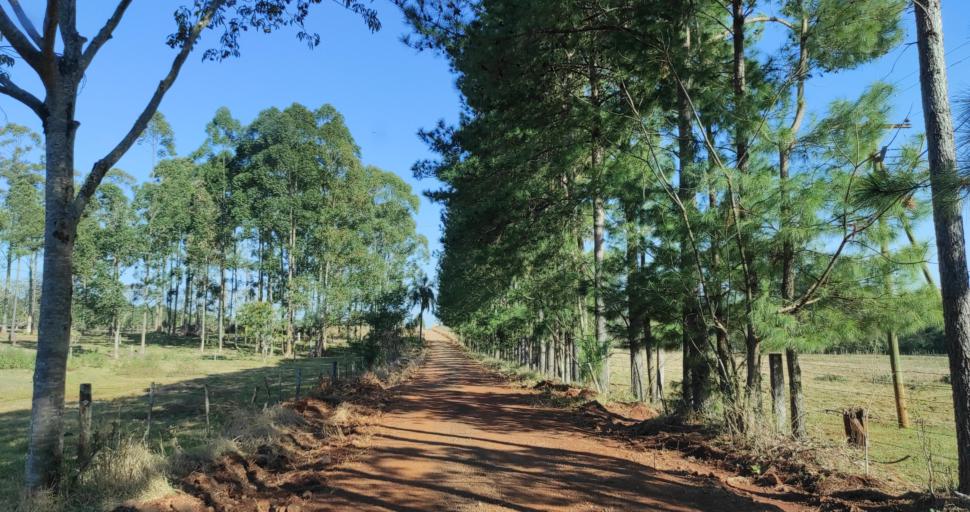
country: AR
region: Misiones
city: Capiovi
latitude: -26.8937
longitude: -55.0417
